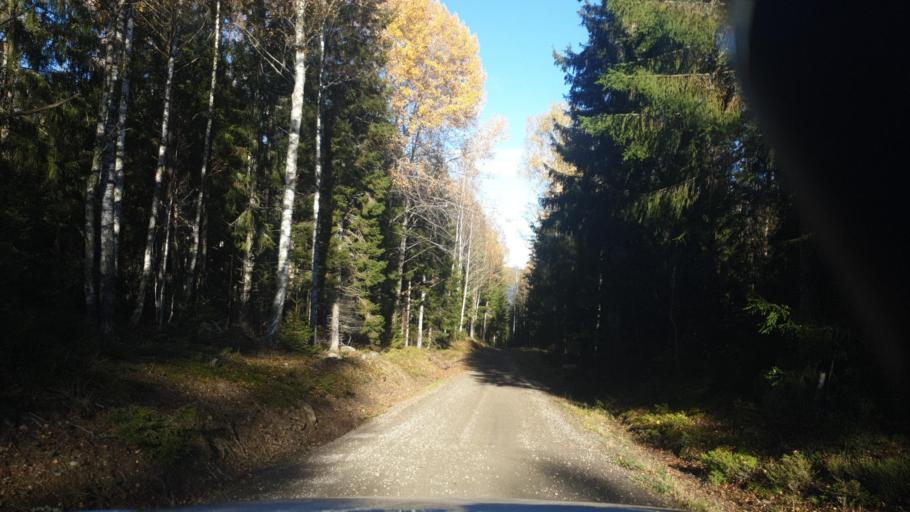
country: SE
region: Vaermland
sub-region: Arvika Kommun
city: Arvika
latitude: 59.5683
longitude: 12.8337
